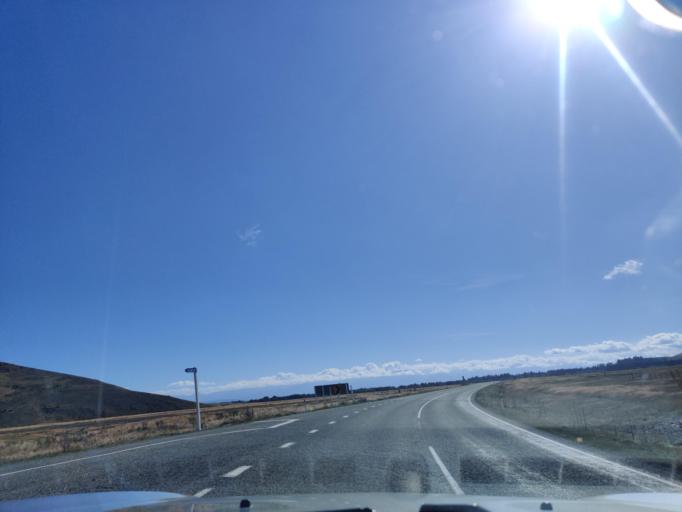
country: NZ
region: Canterbury
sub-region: Timaru District
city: Pleasant Point
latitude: -44.0964
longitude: 170.5659
